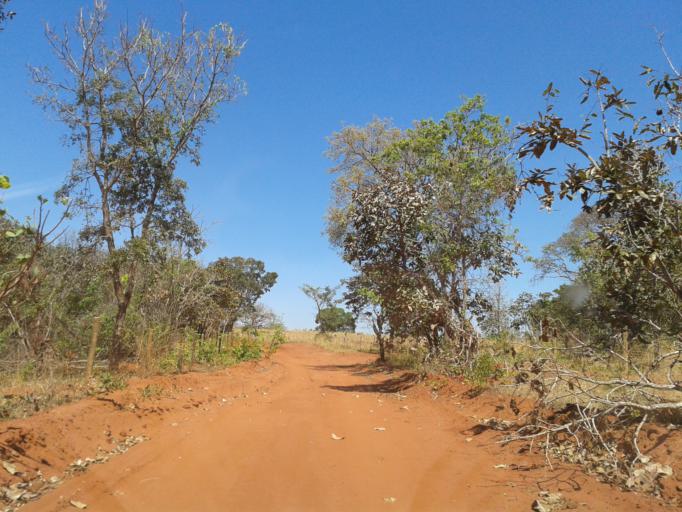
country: BR
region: Minas Gerais
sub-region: Ituiutaba
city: Ituiutaba
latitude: -19.0987
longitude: -49.2699
